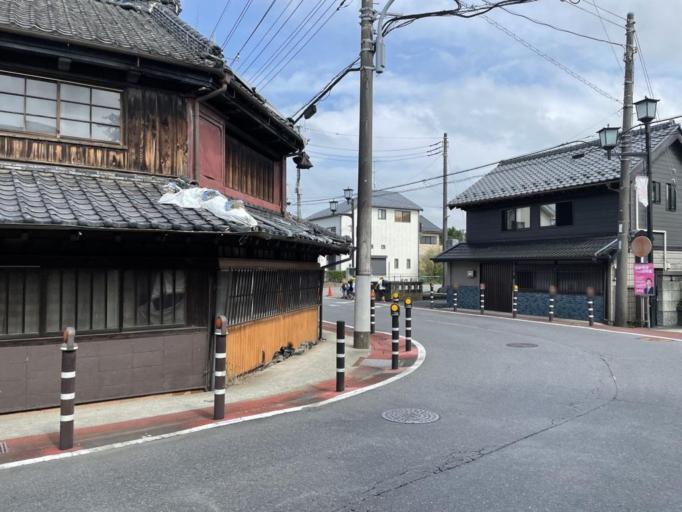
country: JP
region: Chiba
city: Sakura
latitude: 35.7184
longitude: 140.2336
